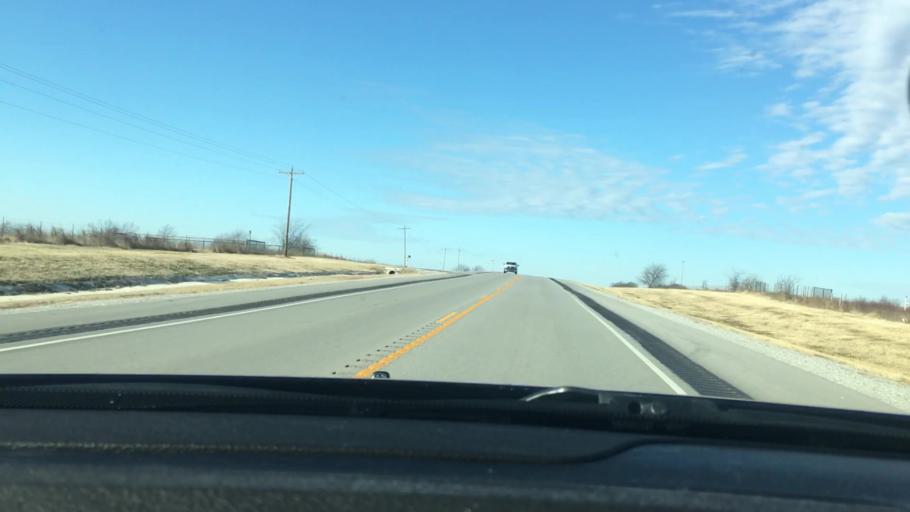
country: US
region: Oklahoma
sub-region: Love County
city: Marietta
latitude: 33.9404
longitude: -97.2272
